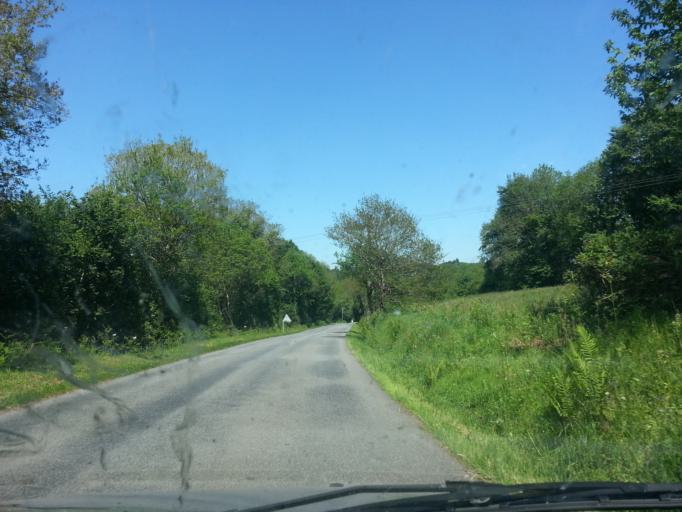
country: FR
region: Brittany
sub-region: Departement du Morbihan
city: Lanvenegen
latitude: 48.0166
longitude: -3.5169
